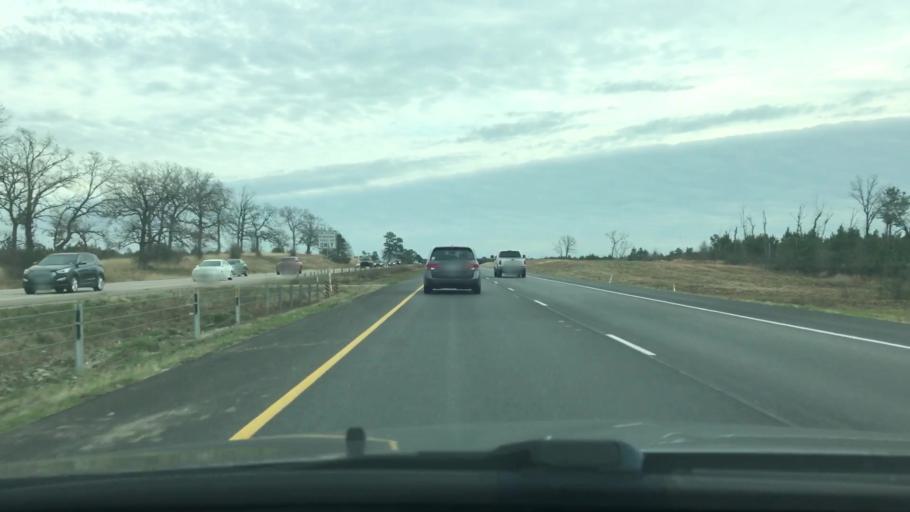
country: US
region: Texas
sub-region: Madison County
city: Madisonville
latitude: 30.8469
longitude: -95.7325
